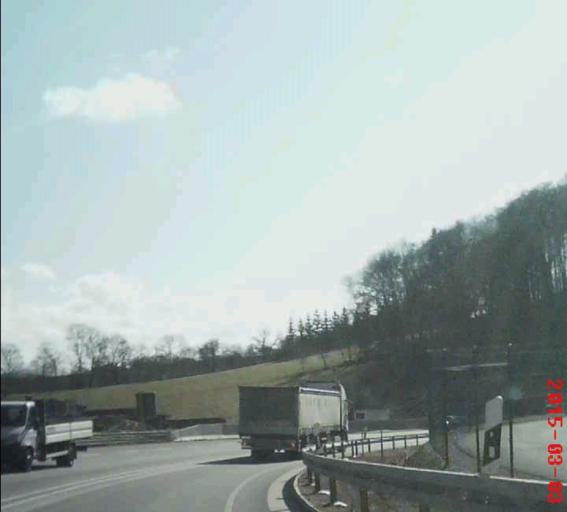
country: DE
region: Thuringia
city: Bad Blankenburg
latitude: 50.7170
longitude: 11.2834
